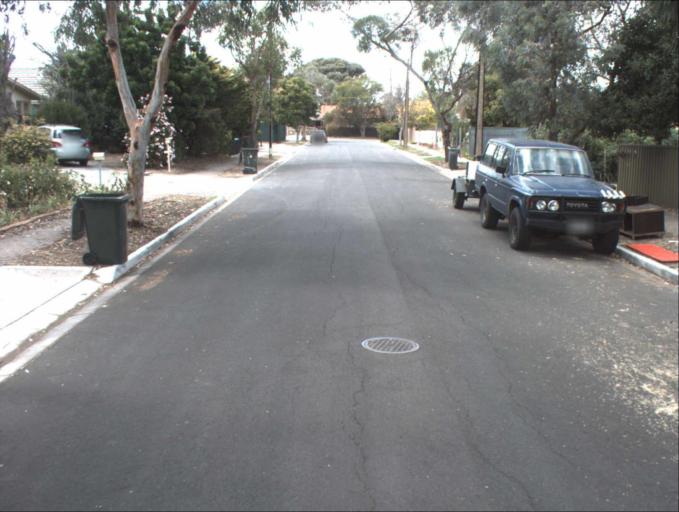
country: AU
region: South Australia
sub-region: Port Adelaide Enfield
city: Gilles Plains
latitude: -34.8558
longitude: 138.6647
